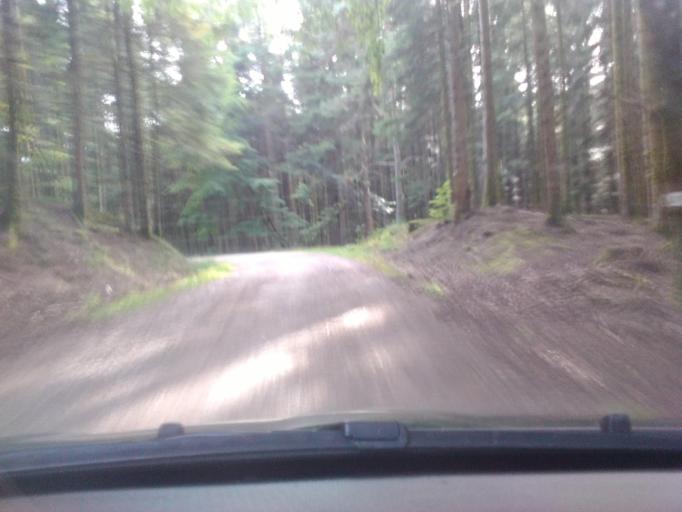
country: FR
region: Lorraine
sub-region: Departement des Vosges
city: Taintrux
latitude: 48.2194
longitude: 6.8790
